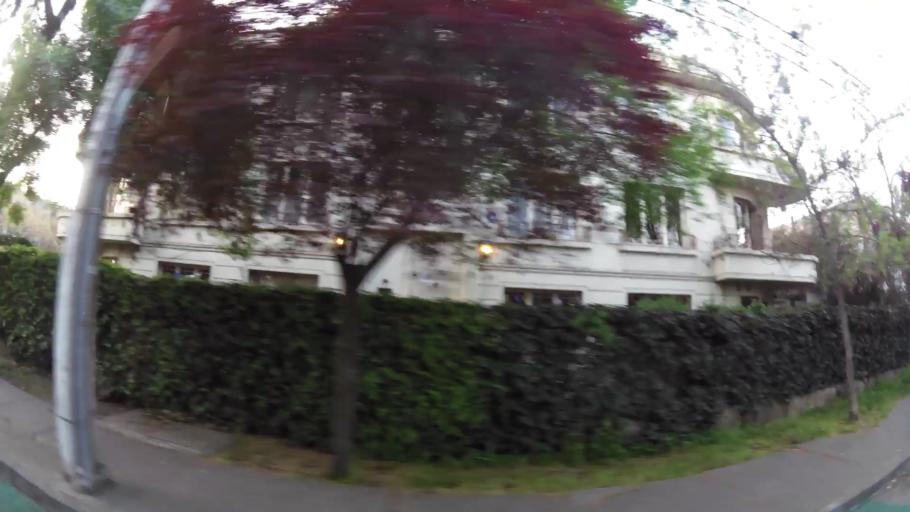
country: CL
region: Santiago Metropolitan
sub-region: Provincia de Santiago
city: Santiago
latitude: -33.4176
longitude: -70.6160
